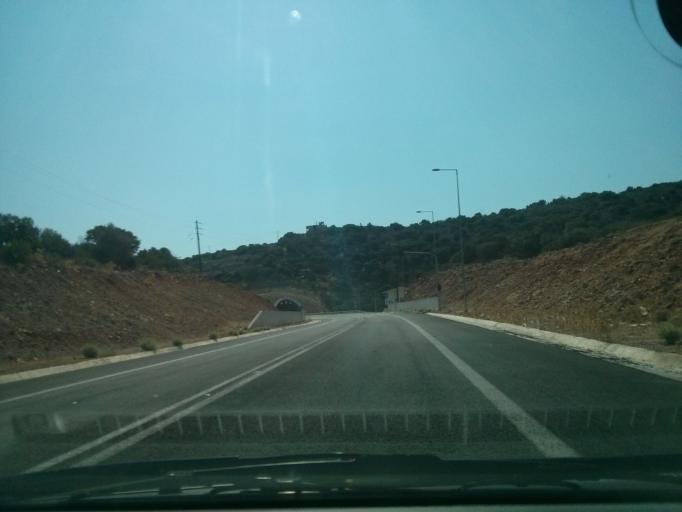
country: GR
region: Crete
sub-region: Nomos Lasithiou
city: Agios Nikolaos
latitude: 35.1628
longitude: 25.7057
